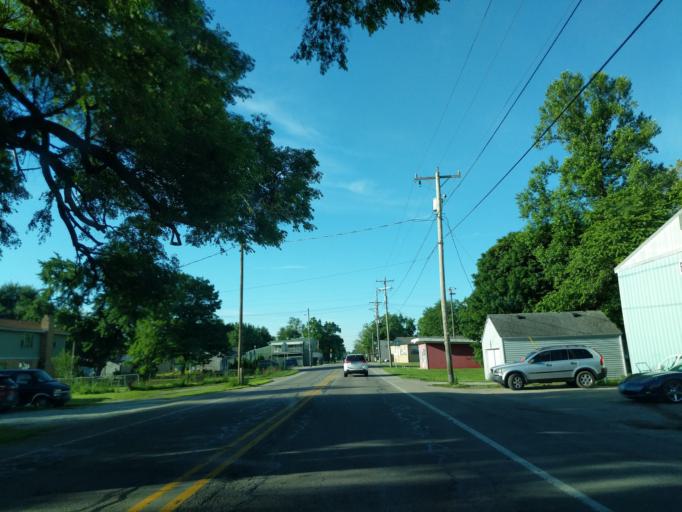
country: US
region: Indiana
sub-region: Hancock County
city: Greenfield
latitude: 39.8585
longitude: -85.7700
